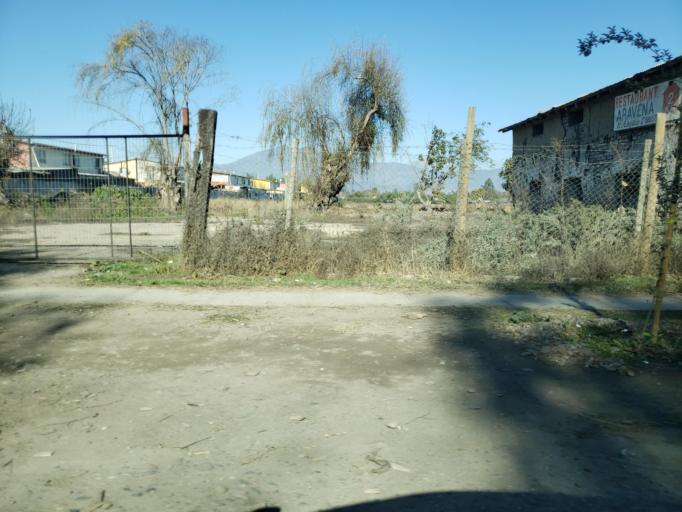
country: CL
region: Santiago Metropolitan
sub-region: Provincia de Talagante
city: El Monte
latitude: -33.6840
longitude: -71.0080
